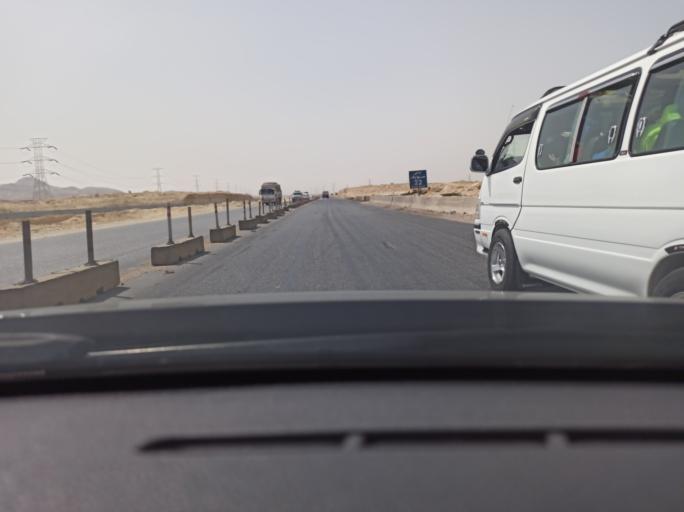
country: EG
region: Muhafazat Bani Suwayf
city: Bush
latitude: 29.1350
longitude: 31.2262
